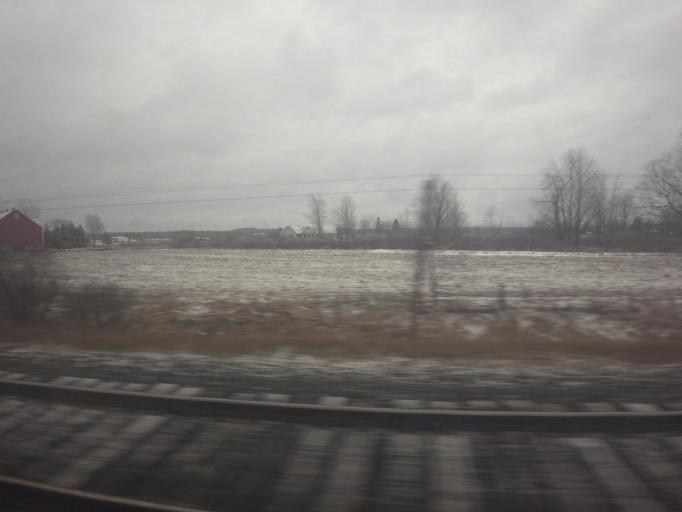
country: CA
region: Ontario
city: Gananoque
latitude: 44.3847
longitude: -76.0614
